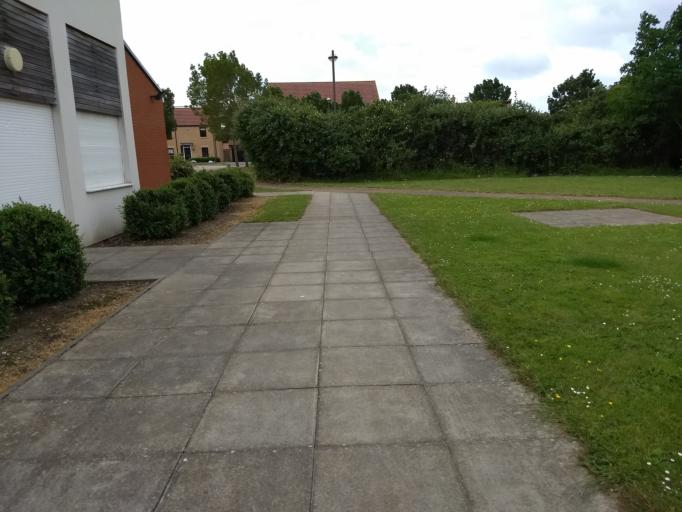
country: GB
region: England
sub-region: Milton Keynes
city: Shenley Church End
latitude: 52.0042
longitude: -0.7989
